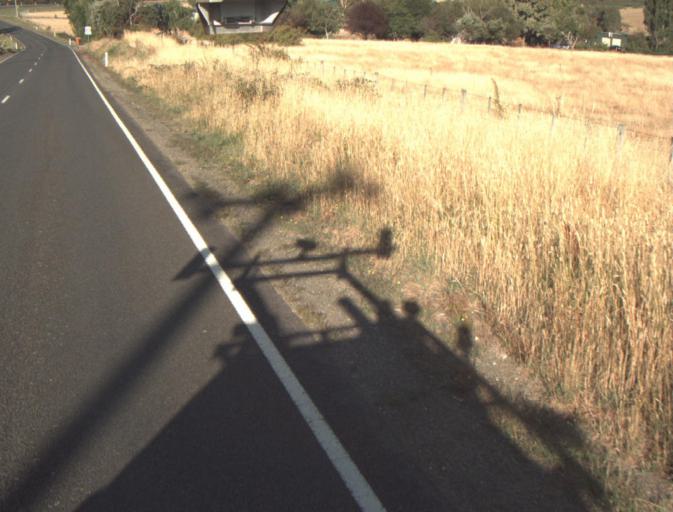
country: AU
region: Tasmania
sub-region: Launceston
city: Newstead
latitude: -41.4353
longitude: 147.2009
